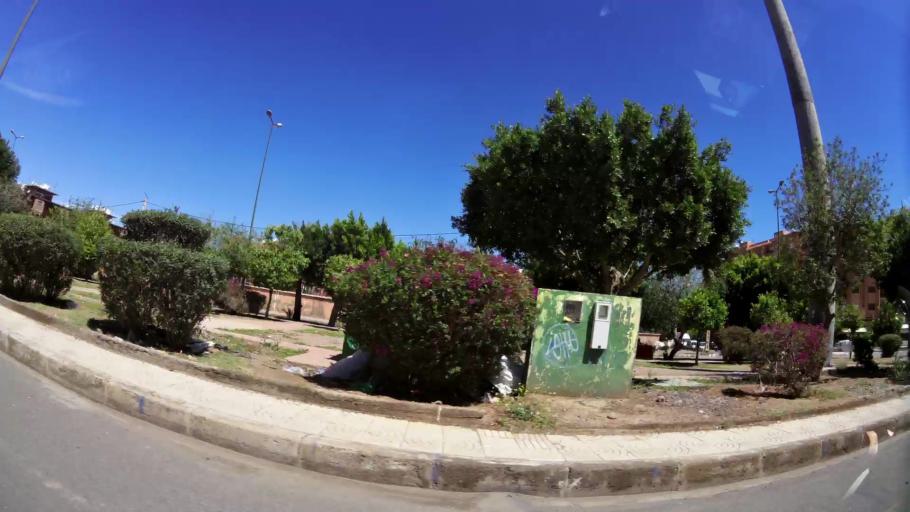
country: MA
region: Marrakech-Tensift-Al Haouz
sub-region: Marrakech
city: Marrakesh
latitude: 31.6341
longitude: -8.0628
